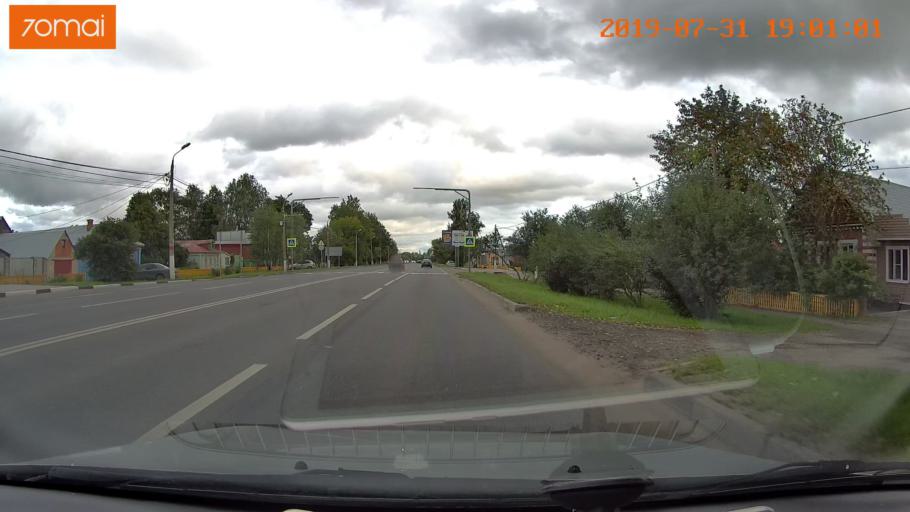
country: RU
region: Moskovskaya
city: Raduzhnyy
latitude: 55.1297
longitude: 38.7281
